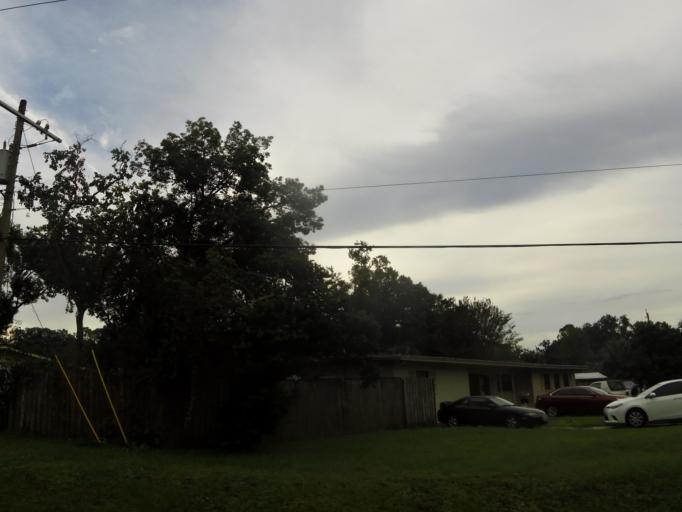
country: US
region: Florida
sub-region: Duval County
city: Jacksonville
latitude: 30.2857
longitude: -81.5971
